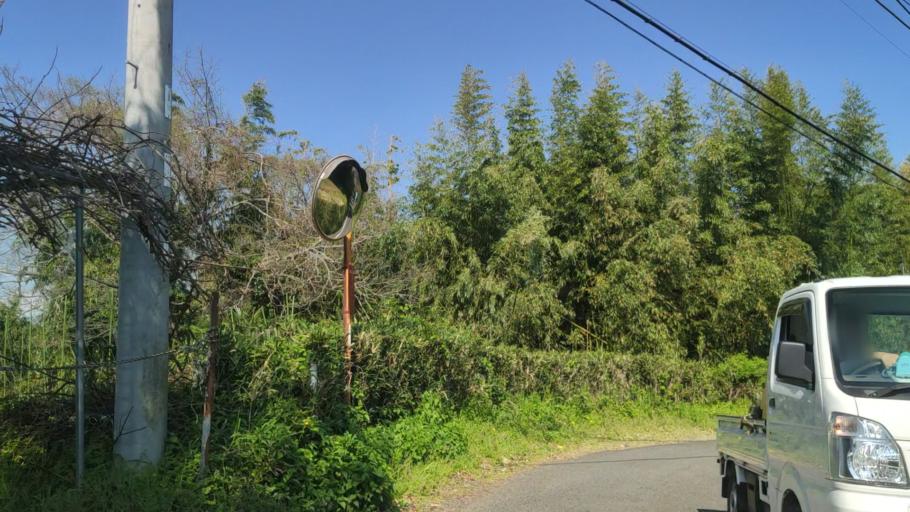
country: JP
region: Kanagawa
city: Ninomiya
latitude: 35.3260
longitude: 139.2571
